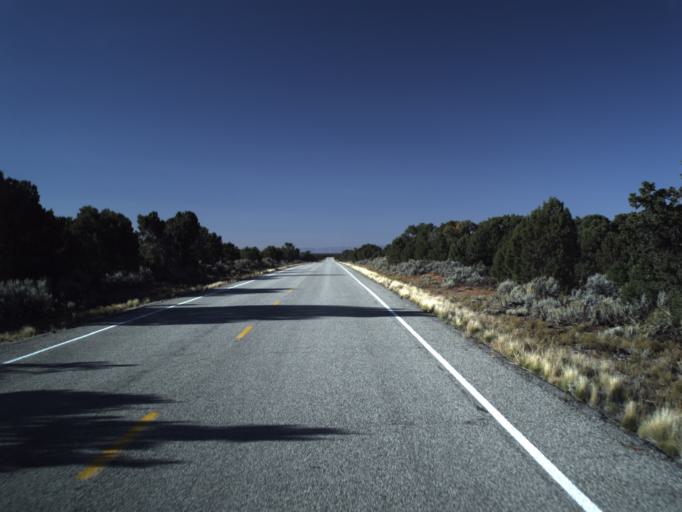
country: US
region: Utah
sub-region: San Juan County
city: Blanding
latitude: 37.5739
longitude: -109.9217
